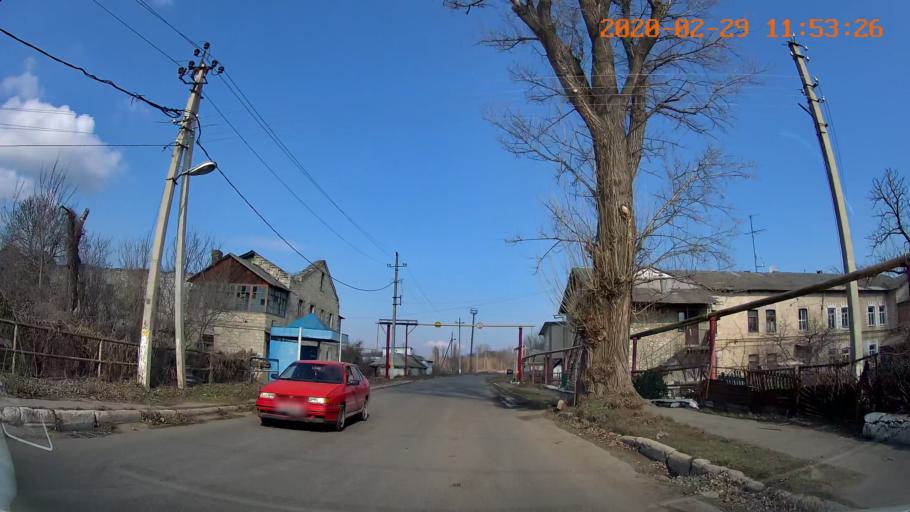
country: MD
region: Telenesti
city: Ribnita
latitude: 47.7775
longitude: 28.9909
